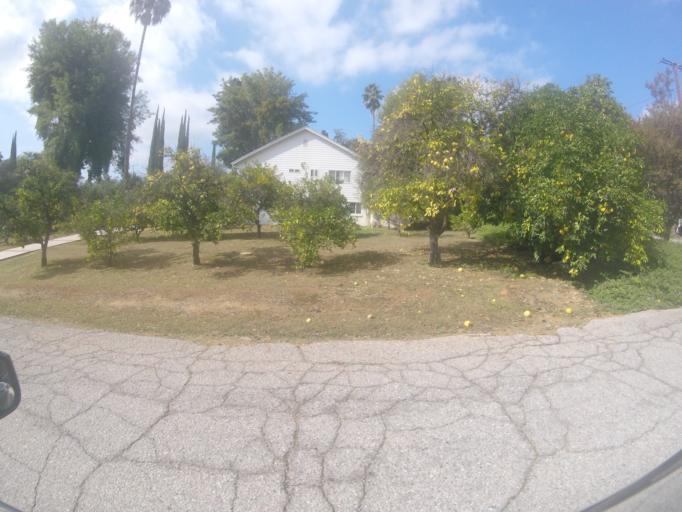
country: US
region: California
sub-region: San Bernardino County
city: Redlands
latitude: 34.0406
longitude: -117.1595
